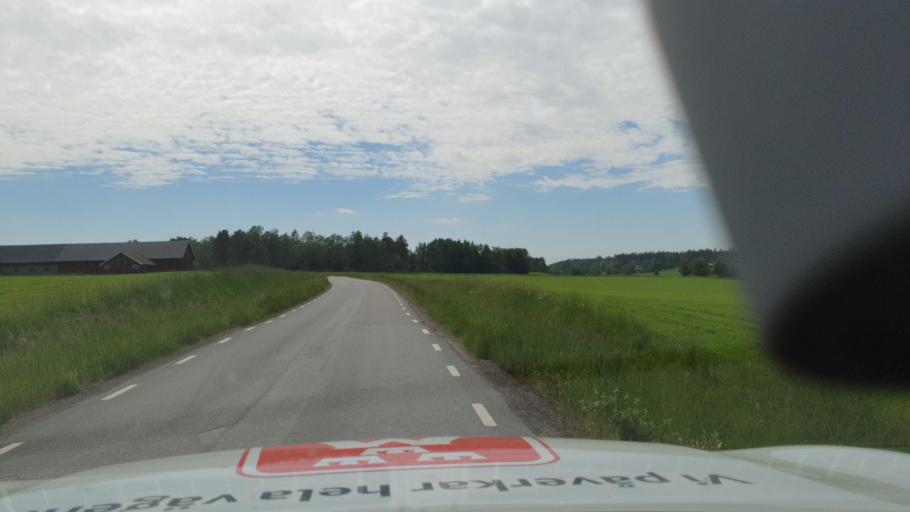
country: SE
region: Vaestra Goetaland
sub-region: Vanersborgs Kommun
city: Vargon
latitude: 58.2848
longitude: 12.5181
